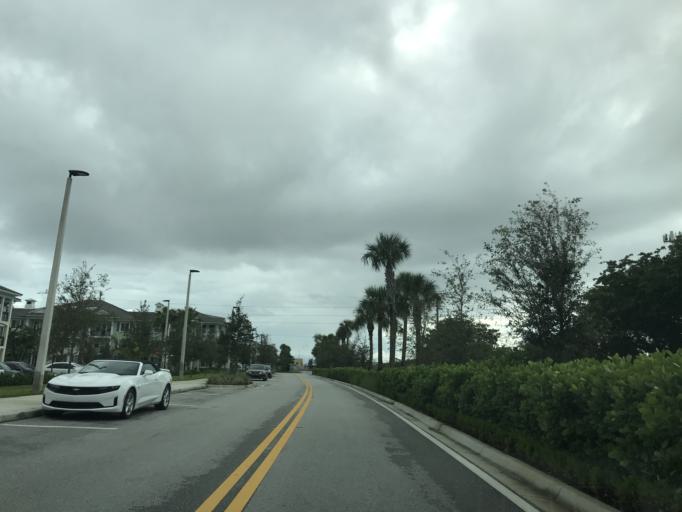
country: US
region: Florida
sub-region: Palm Beach County
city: Delray Beach
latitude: 26.4668
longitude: -80.0909
